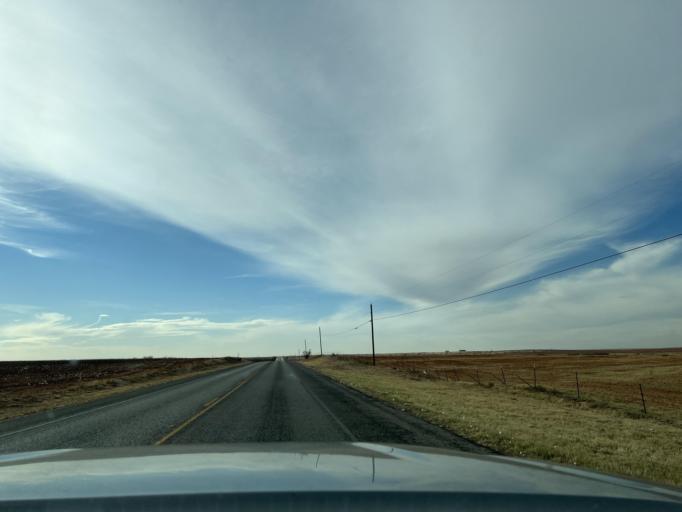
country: US
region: Texas
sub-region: Fisher County
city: Roby
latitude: 32.7413
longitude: -100.4650
